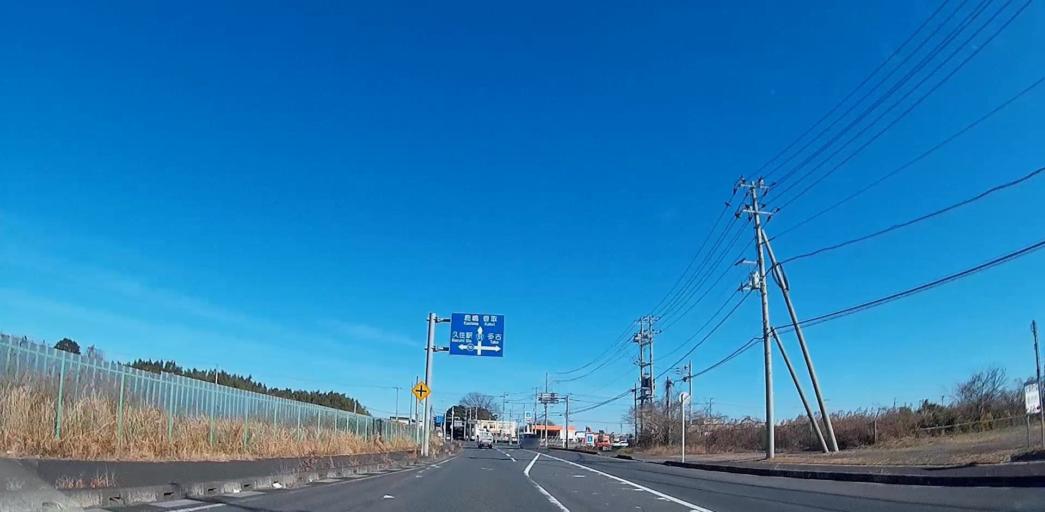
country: JP
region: Chiba
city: Narita
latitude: 35.8064
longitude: 140.3822
